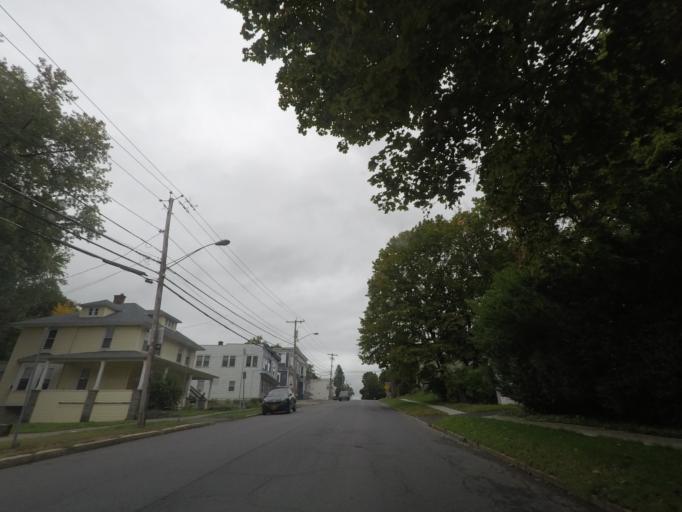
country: US
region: New York
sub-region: Rensselaer County
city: Rensselaer
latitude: 42.6574
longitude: -73.7307
